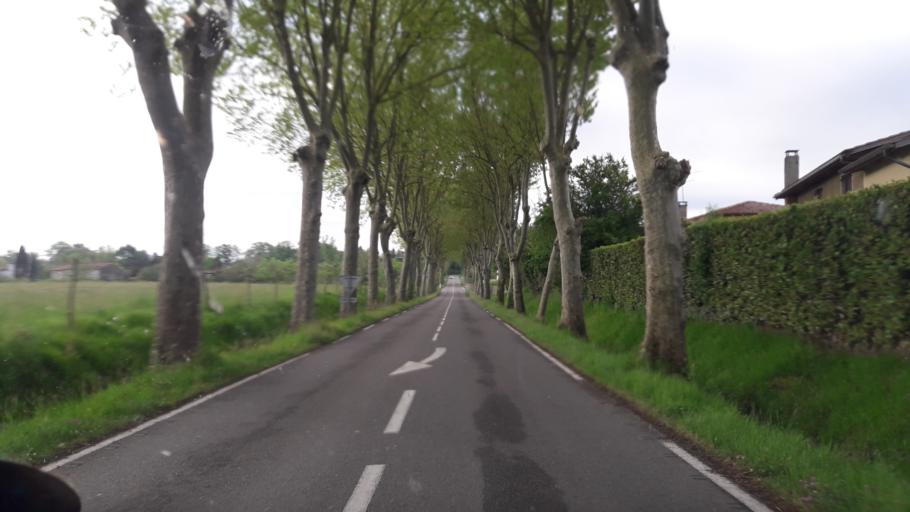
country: FR
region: Midi-Pyrenees
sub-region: Departement de la Haute-Garonne
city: Cazeres
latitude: 43.2032
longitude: 1.0904
